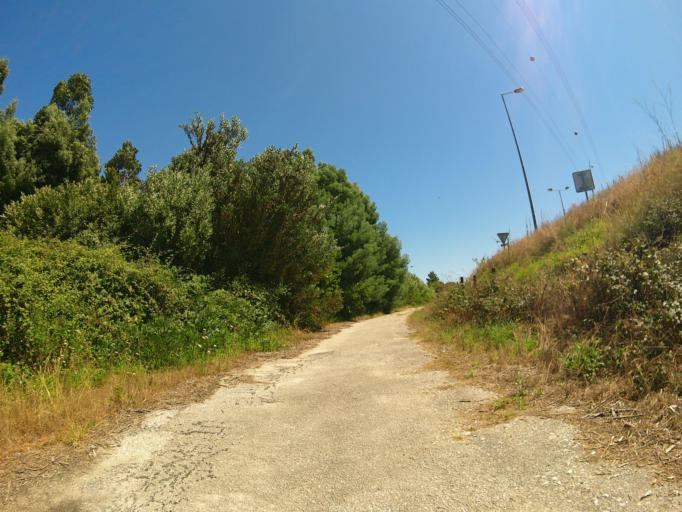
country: PT
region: Viana do Castelo
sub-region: Viana do Castelo
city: Darque
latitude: 41.6845
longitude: -8.7745
